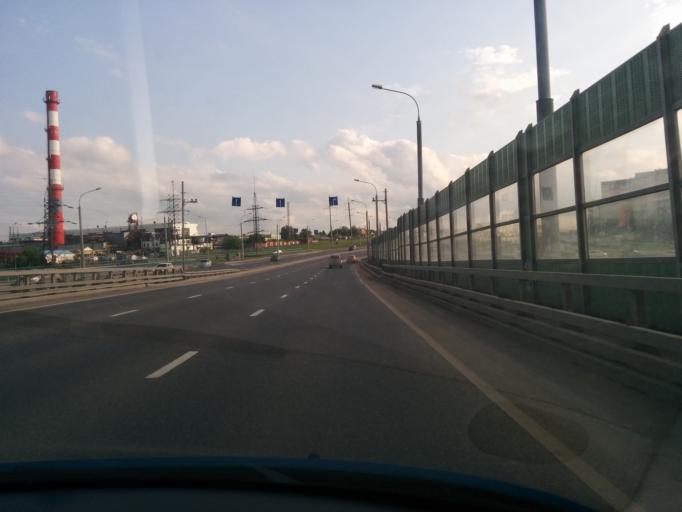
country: RU
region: Perm
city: Perm
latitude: 58.0022
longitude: 56.3155
